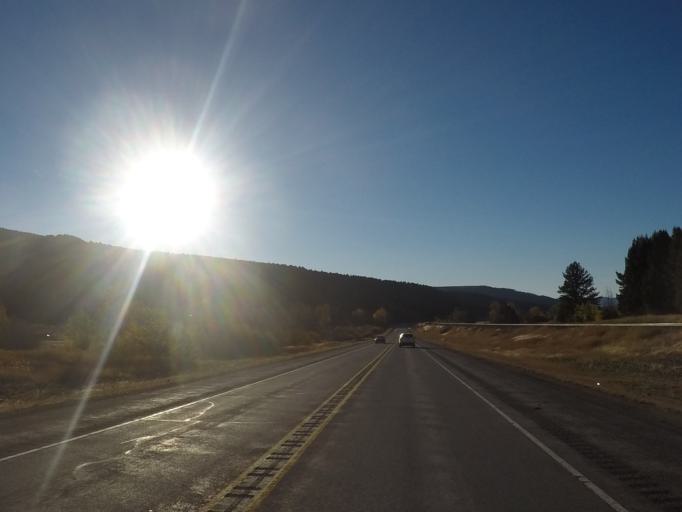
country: US
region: Montana
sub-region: Lewis and Clark County
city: Helena West Side
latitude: 46.5568
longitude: -112.4022
